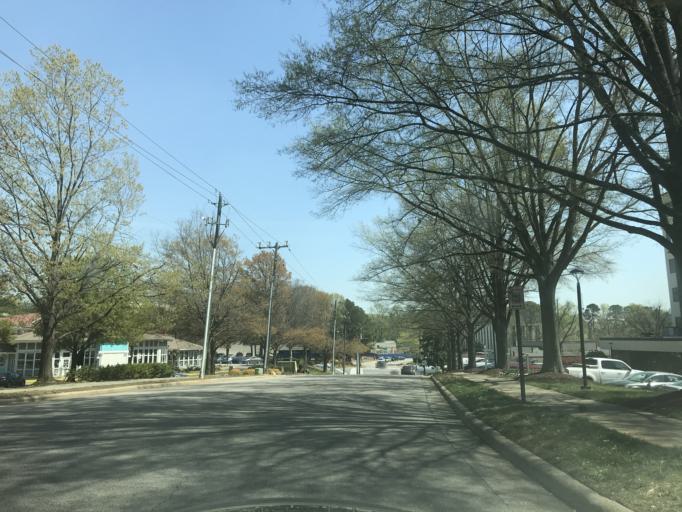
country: US
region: North Carolina
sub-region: Wake County
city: Raleigh
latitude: 35.8281
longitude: -78.6218
